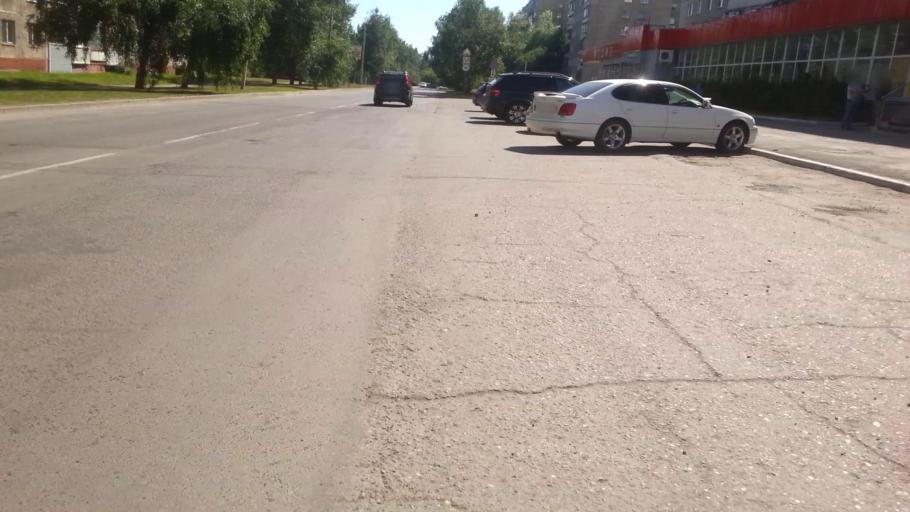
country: RU
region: Altai Krai
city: Novosilikatnyy
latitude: 53.3655
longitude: 83.6680
